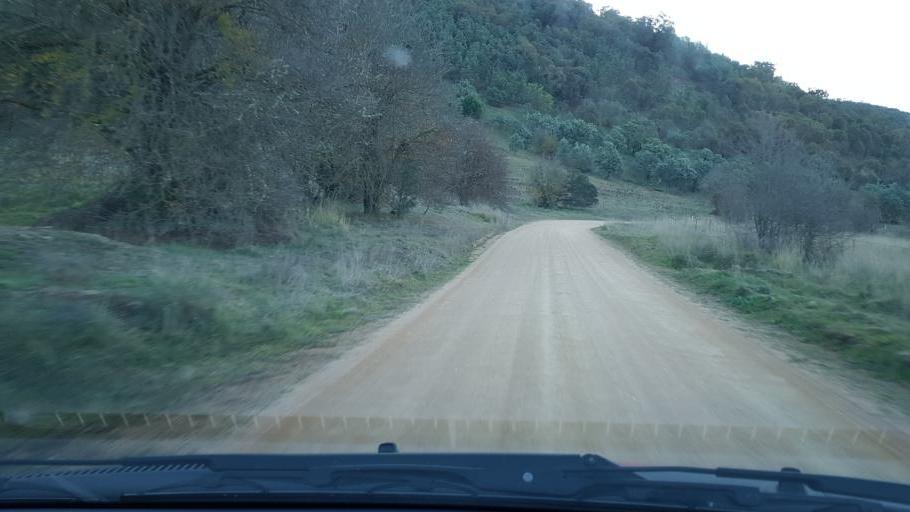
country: AU
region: New South Wales
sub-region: Palerang
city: Bungendore
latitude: -35.1904
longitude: 149.3987
